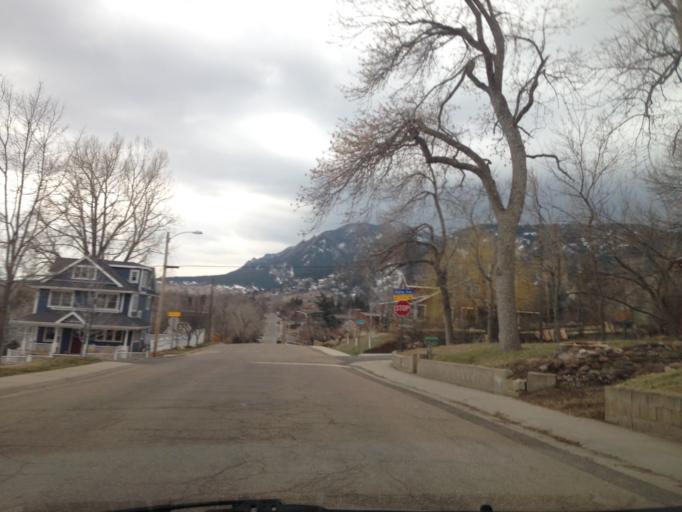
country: US
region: Colorado
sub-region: Boulder County
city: Boulder
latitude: 40.0260
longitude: -105.2916
